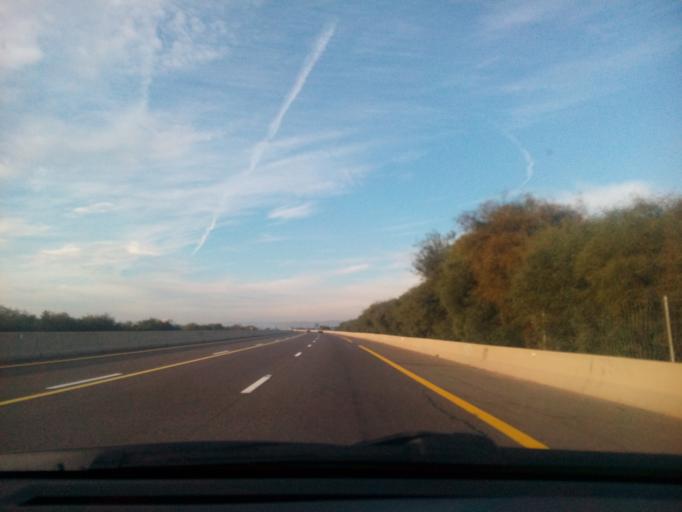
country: DZ
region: Relizane
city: Relizane
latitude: 35.7924
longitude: 0.4365
